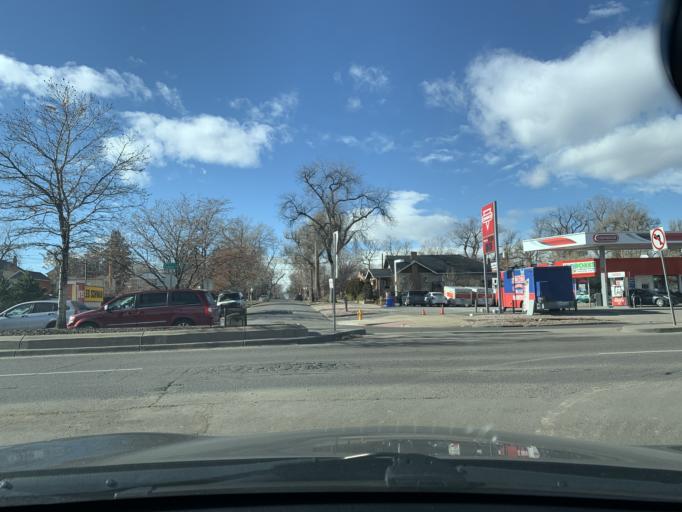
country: US
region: Colorado
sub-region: Jefferson County
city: Edgewater
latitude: 39.7488
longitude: -105.0250
